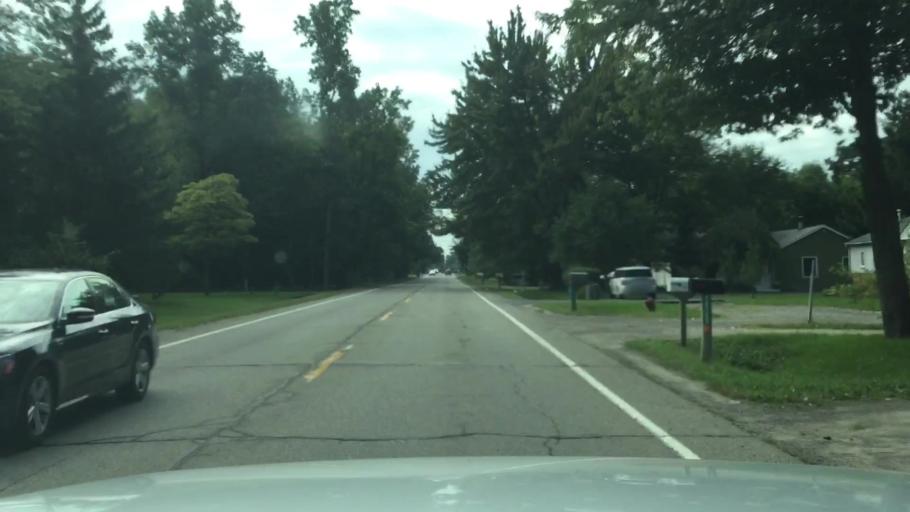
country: US
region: Michigan
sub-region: Wayne County
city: Belleville
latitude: 42.1668
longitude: -83.4826
